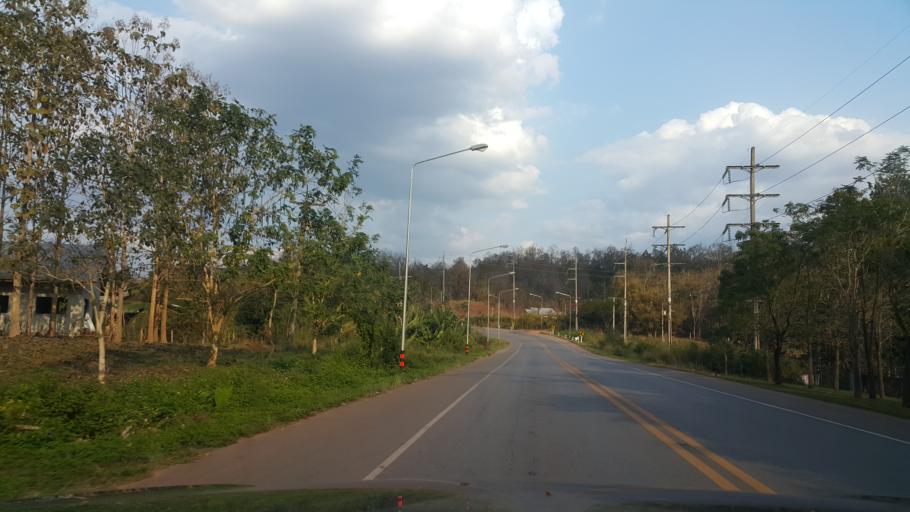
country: TH
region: Loei
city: Dan Sai
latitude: 17.2939
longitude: 101.1921
